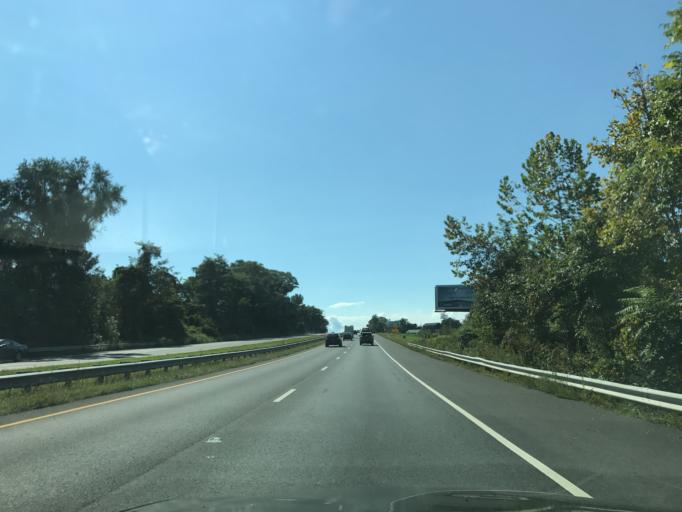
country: US
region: Maryland
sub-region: Cecil County
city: Perryville
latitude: 39.5809
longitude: -76.0309
